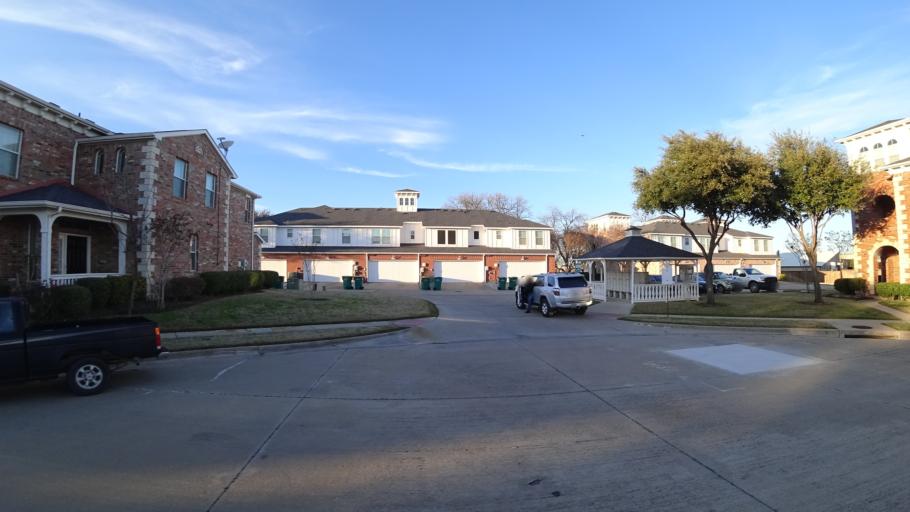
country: US
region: Texas
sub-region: Denton County
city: Lewisville
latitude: 33.0451
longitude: -96.9877
